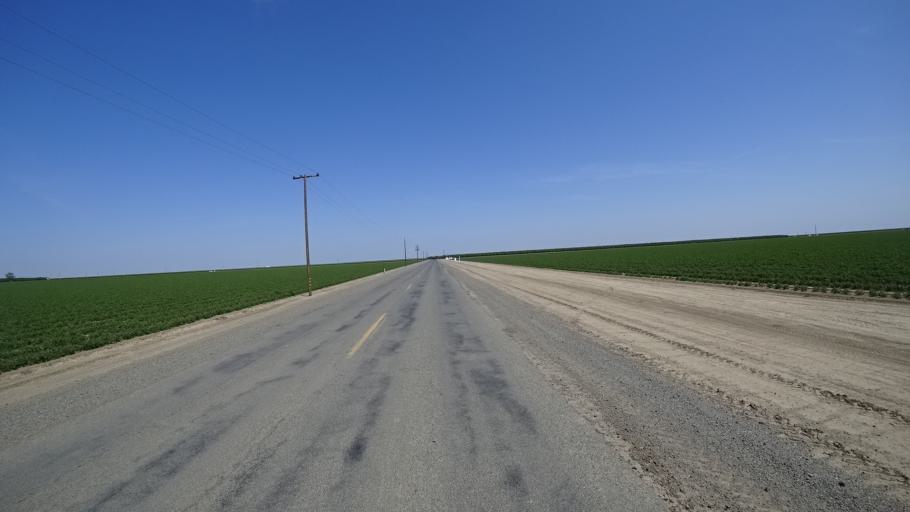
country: US
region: California
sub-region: Fresno County
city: Huron
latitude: 36.1323
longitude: -120.0037
